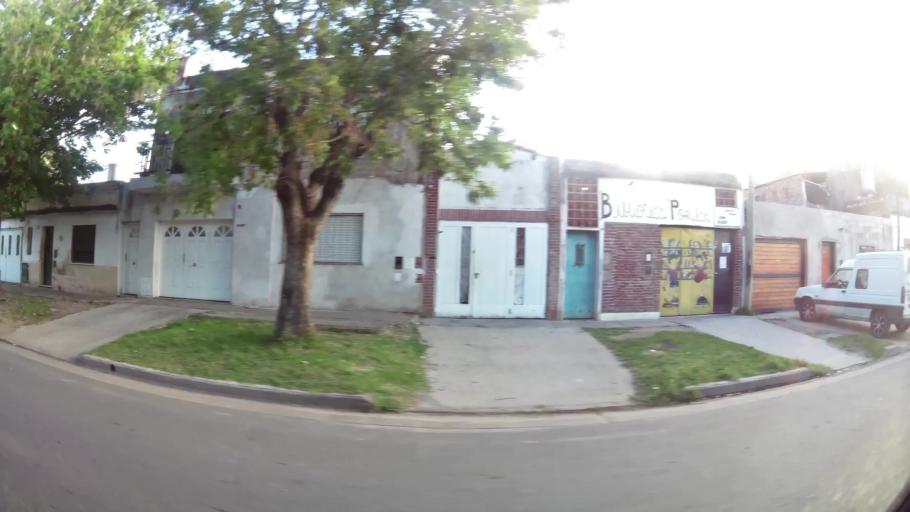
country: AR
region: Santa Fe
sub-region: Departamento de Rosario
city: Rosario
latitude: -32.9806
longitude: -60.6651
